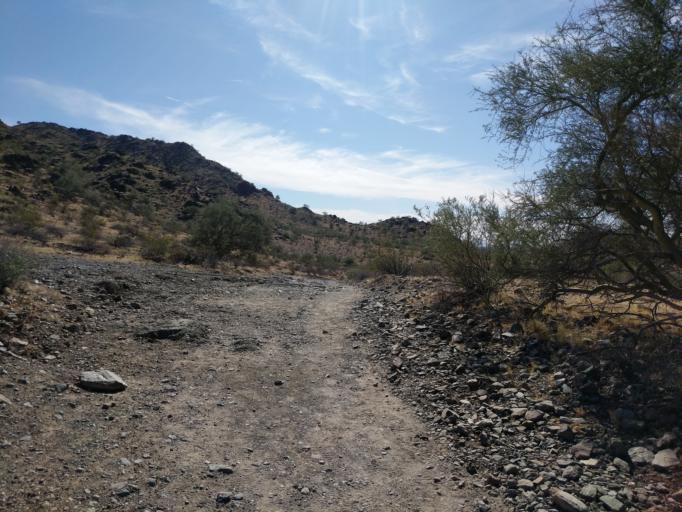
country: US
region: Arizona
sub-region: Maricopa County
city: Glendale
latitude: 33.5919
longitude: -112.0758
